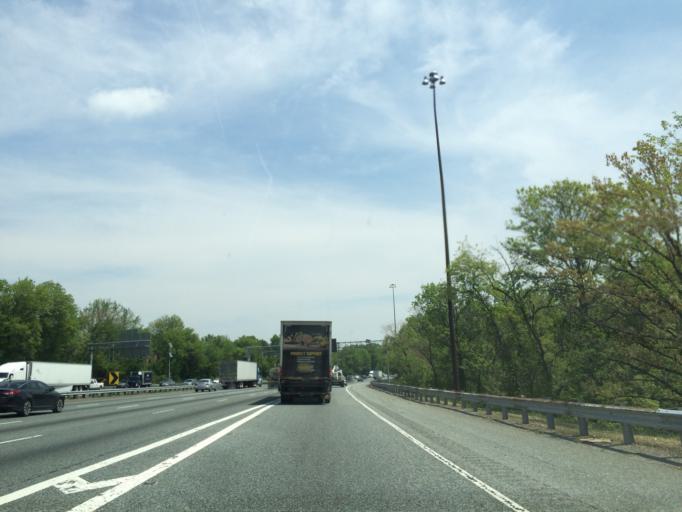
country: US
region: Maryland
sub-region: Baltimore County
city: Arbutus
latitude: 39.2380
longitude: -76.7059
